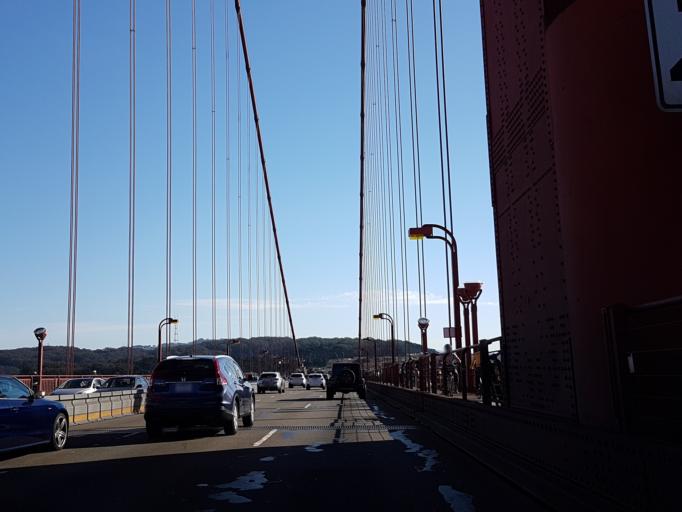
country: US
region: California
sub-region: Marin County
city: Sausalito
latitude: 37.8153
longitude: -122.4780
